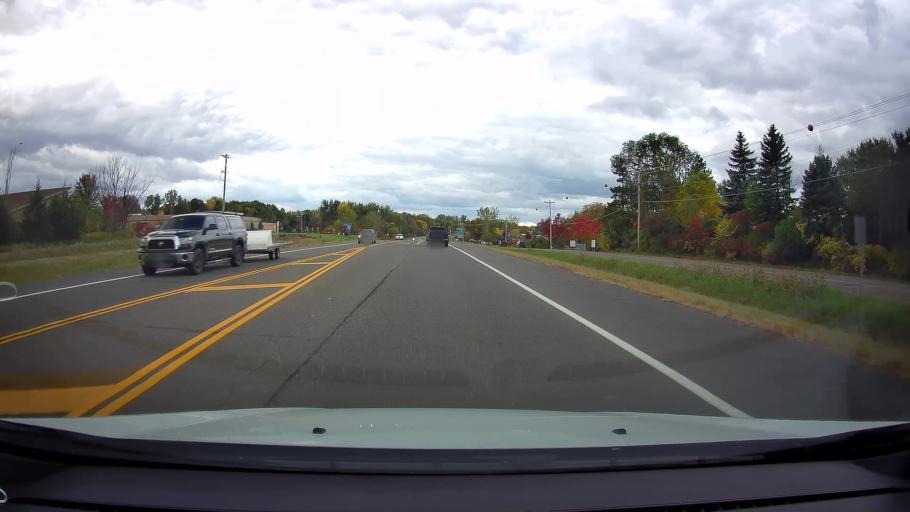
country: US
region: Minnesota
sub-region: Chisago County
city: Lindstrom
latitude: 45.3849
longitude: -92.8686
